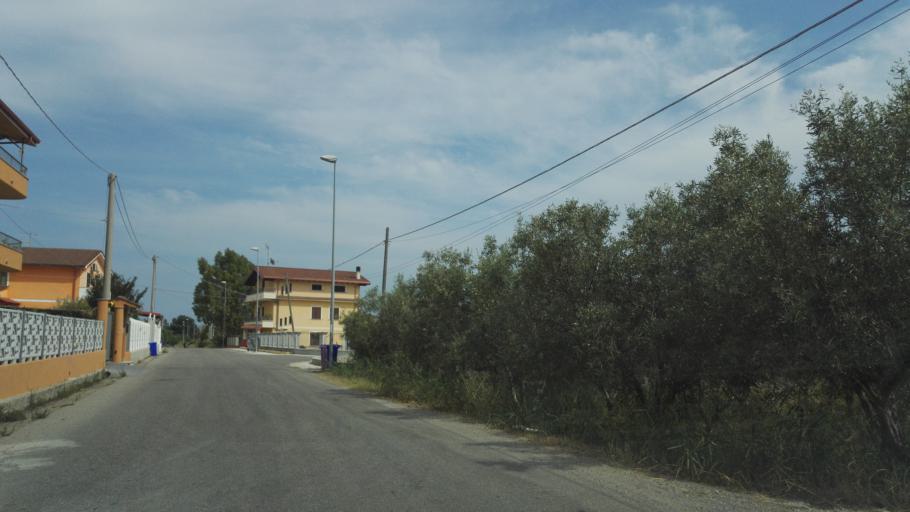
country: IT
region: Calabria
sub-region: Provincia di Reggio Calabria
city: Monasterace
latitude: 38.4305
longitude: 16.5346
